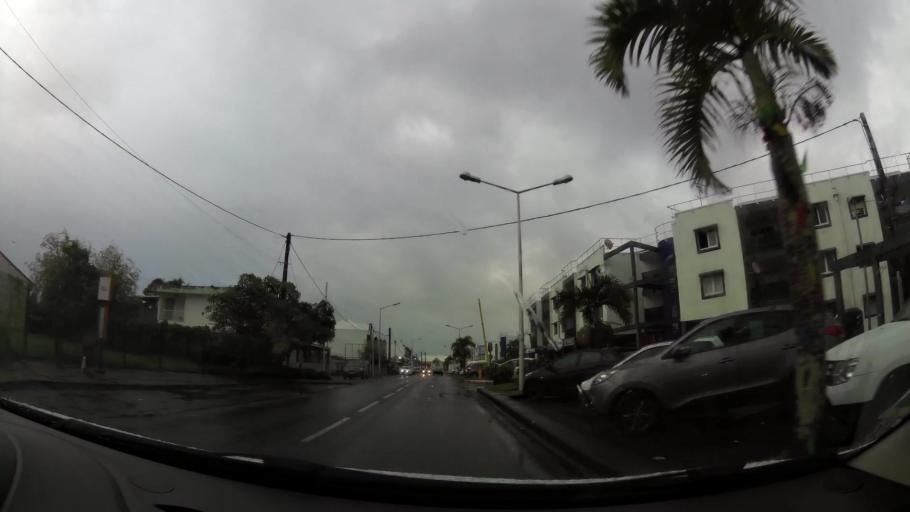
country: RE
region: Reunion
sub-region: Reunion
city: Saint-Benoit
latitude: -21.0397
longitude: 55.7192
